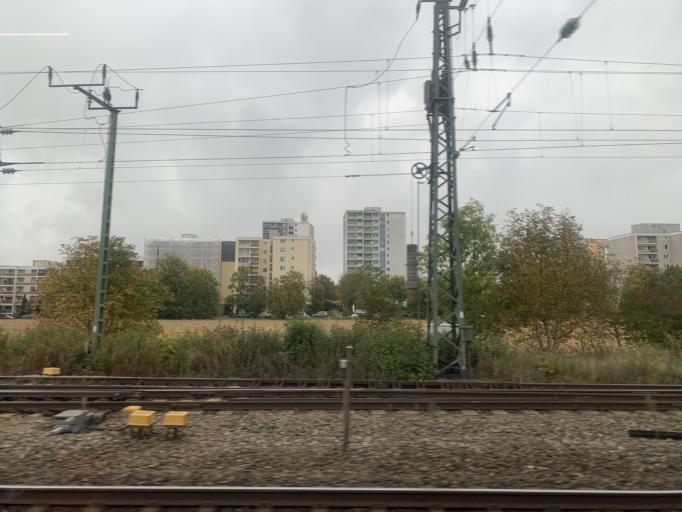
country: DE
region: Bavaria
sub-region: Upper Bavaria
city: Oberschleissheim
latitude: 48.2099
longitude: 11.5411
